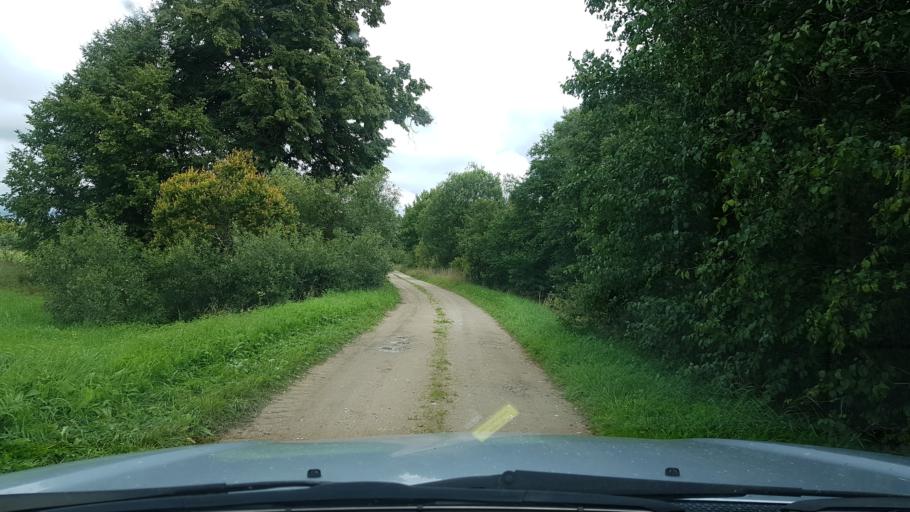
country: EE
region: Harju
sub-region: Rae vald
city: Vaida
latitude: 59.2755
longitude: 24.9644
